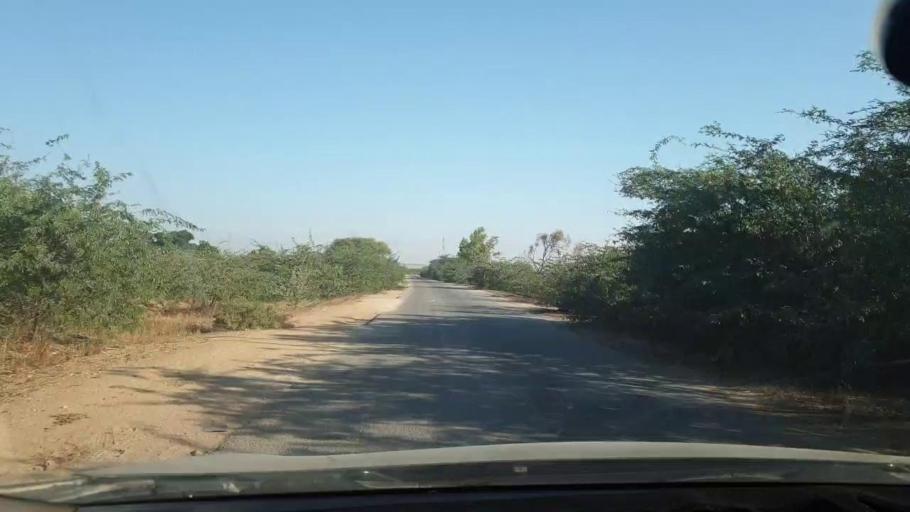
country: PK
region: Sindh
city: Malir Cantonment
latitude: 25.1527
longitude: 67.1904
